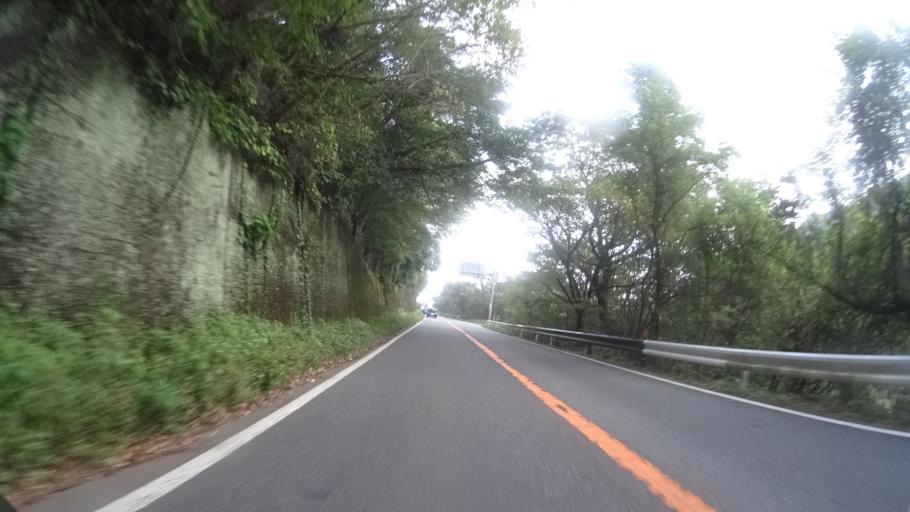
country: JP
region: Oita
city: Beppu
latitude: 33.2706
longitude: 131.4165
